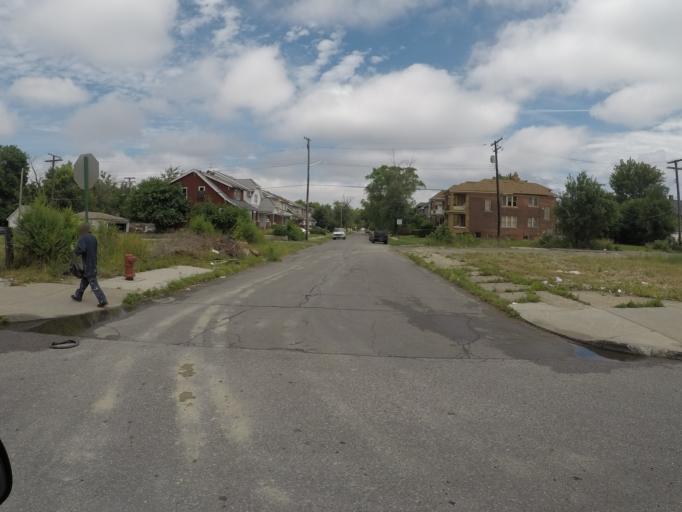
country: US
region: Michigan
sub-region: Wayne County
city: Dearborn
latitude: 42.3450
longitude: -83.1416
